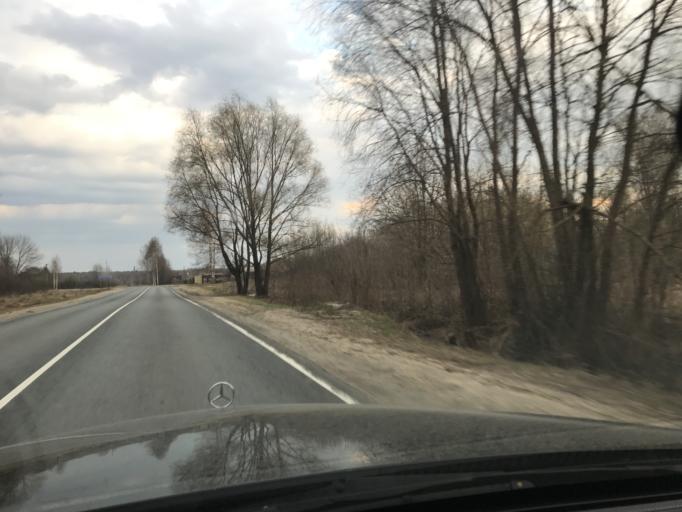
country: RU
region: Vladimir
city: Murom
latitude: 55.6275
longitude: 41.8855
